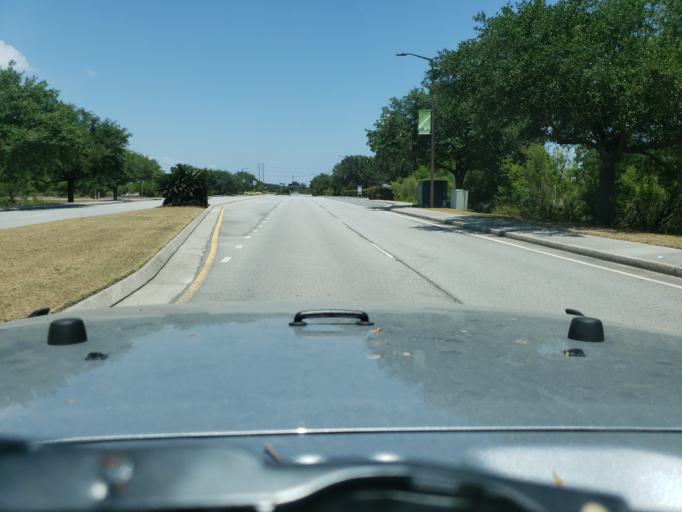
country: US
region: Georgia
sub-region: Chatham County
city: Savannah
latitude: 32.0917
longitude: -81.0899
